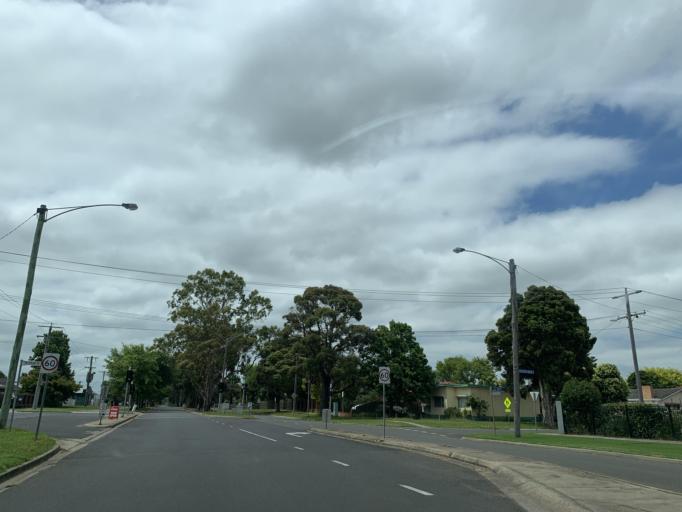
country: AU
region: Victoria
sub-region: Wellington
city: Sale
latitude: -38.1045
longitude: 147.0826
